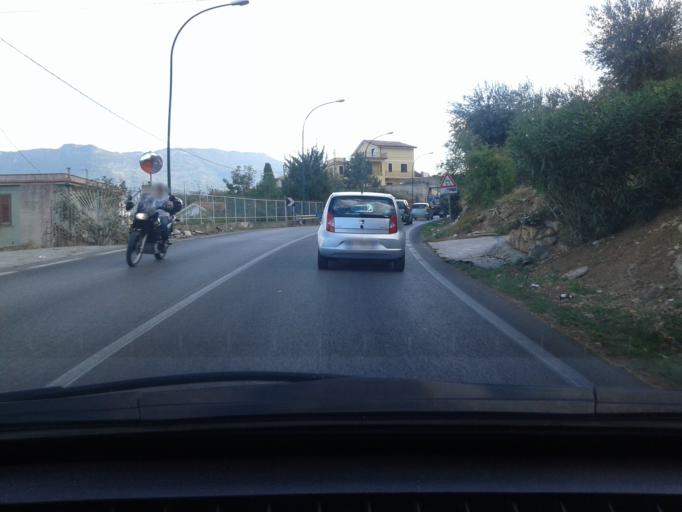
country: IT
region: Sicily
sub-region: Palermo
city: Monreale
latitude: 38.0840
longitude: 13.3008
